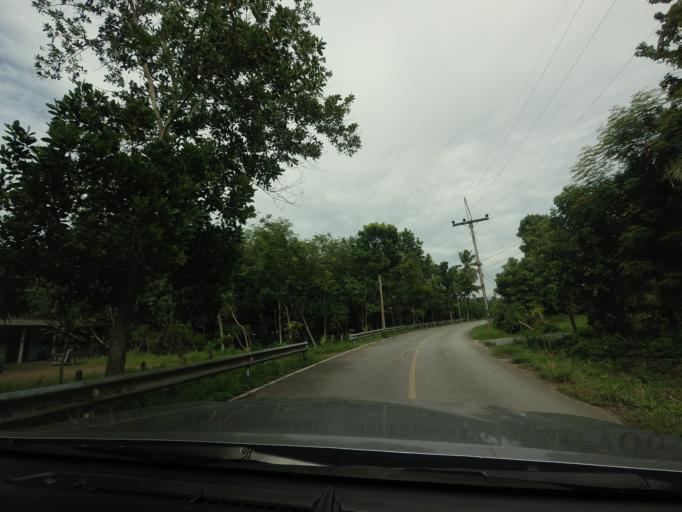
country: TH
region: Nakhon Si Thammarat
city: Phra Phrom
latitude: 8.2824
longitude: 99.9134
